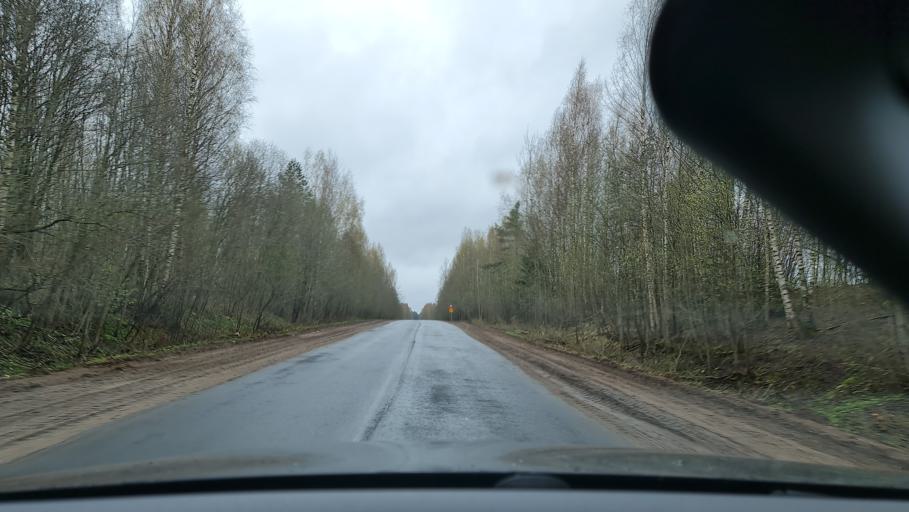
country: RU
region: Novgorod
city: Demyansk
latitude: 57.7394
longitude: 32.5735
